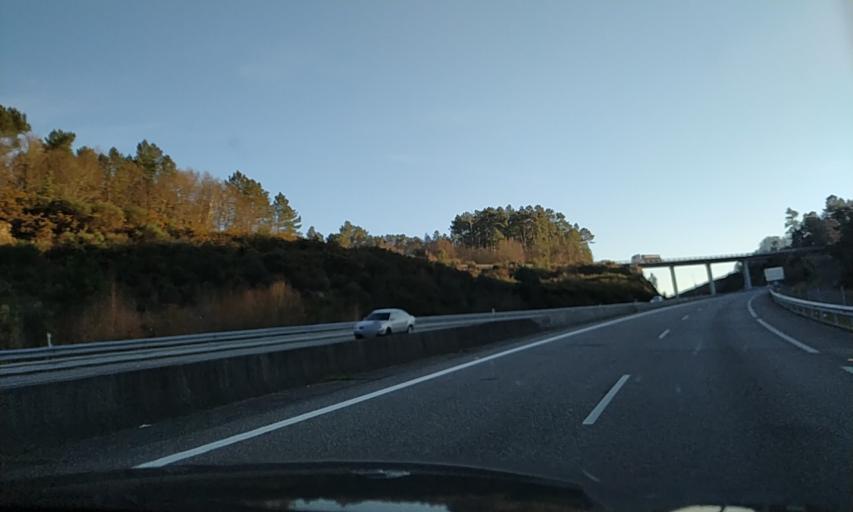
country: ES
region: Galicia
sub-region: Provincia de Ourense
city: Cea
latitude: 42.4562
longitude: -8.0235
